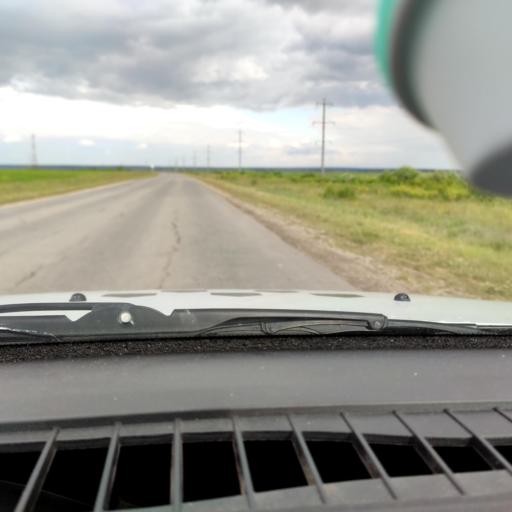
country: RU
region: Perm
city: Orda
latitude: 57.1904
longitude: 56.8655
